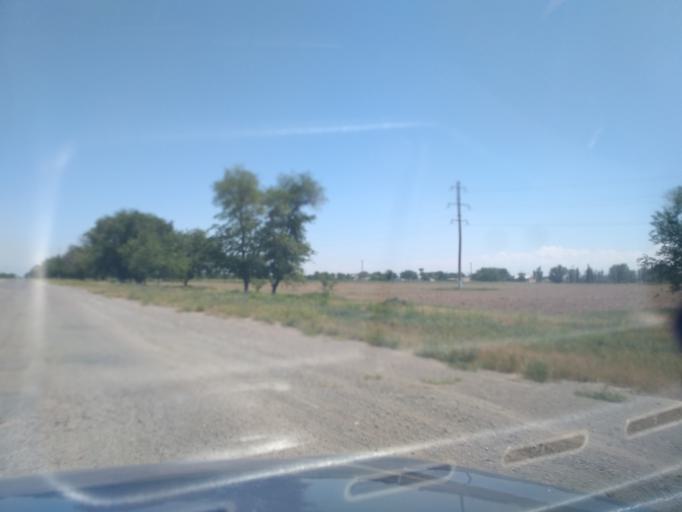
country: TJ
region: Viloyati Sughd
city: Zafarobod
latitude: 40.2199
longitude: 68.9116
